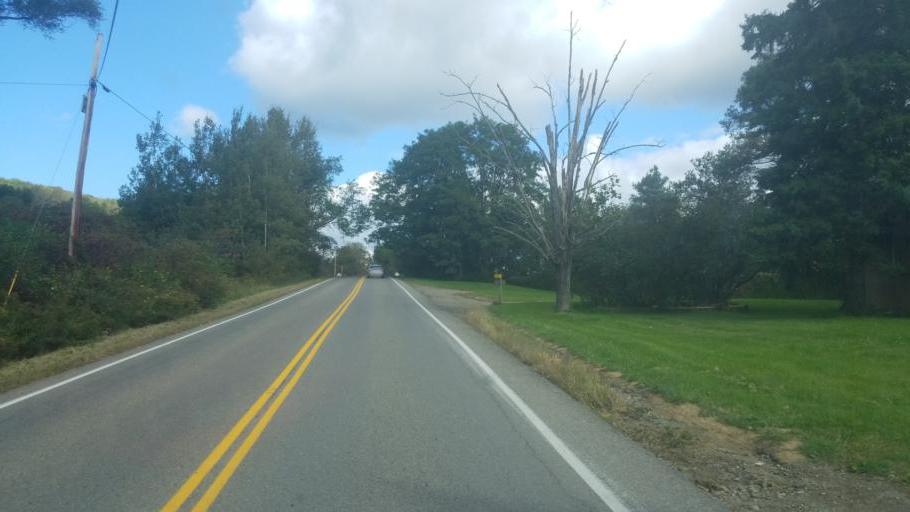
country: US
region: New York
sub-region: Allegany County
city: Cuba
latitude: 42.2181
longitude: -78.3111
